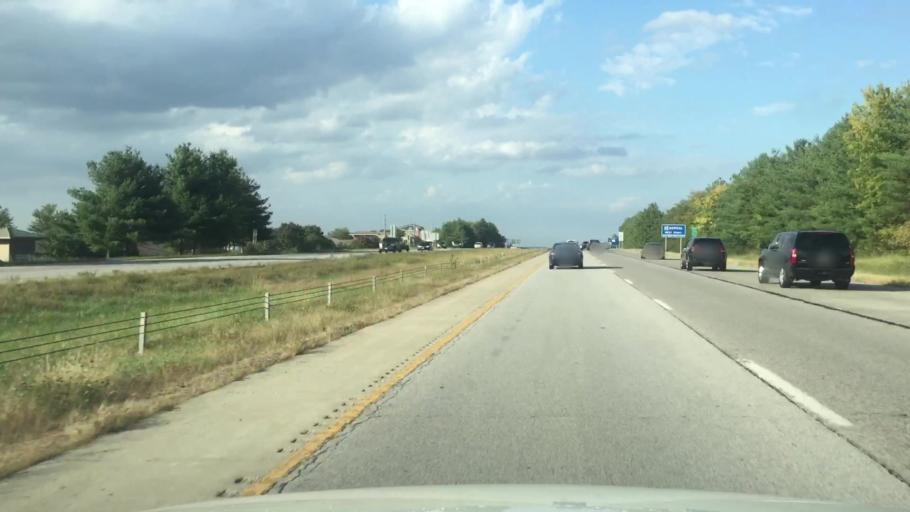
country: US
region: Missouri
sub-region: Jackson County
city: Lees Summit
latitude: 38.9735
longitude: -94.3573
